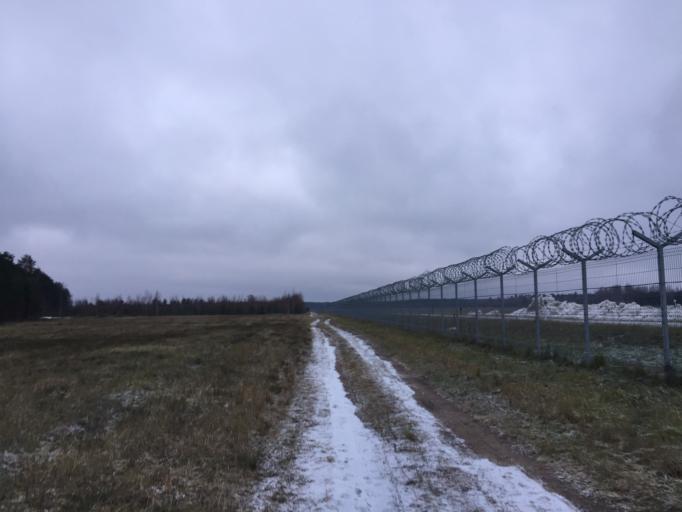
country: LV
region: Babite
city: Pinki
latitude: 56.9076
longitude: 23.9740
